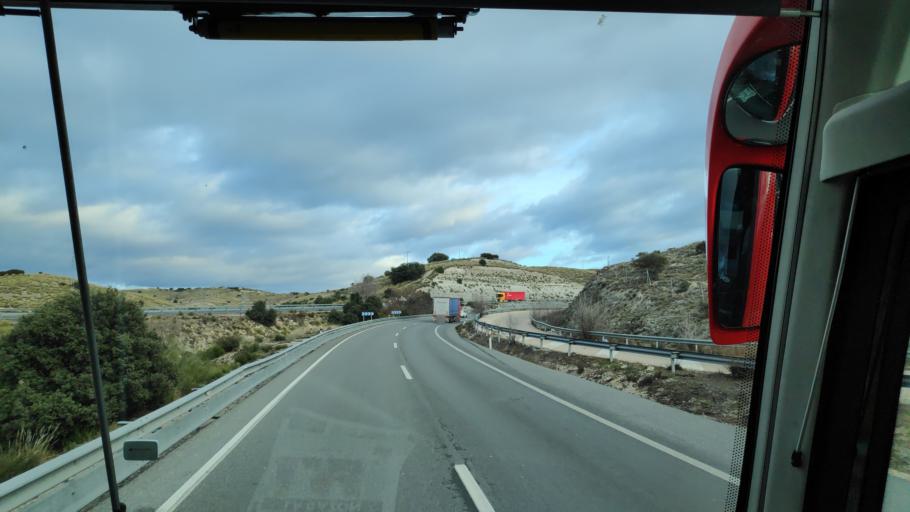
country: ES
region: Madrid
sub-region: Provincia de Madrid
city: Tielmes
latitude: 40.2080
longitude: -3.3182
